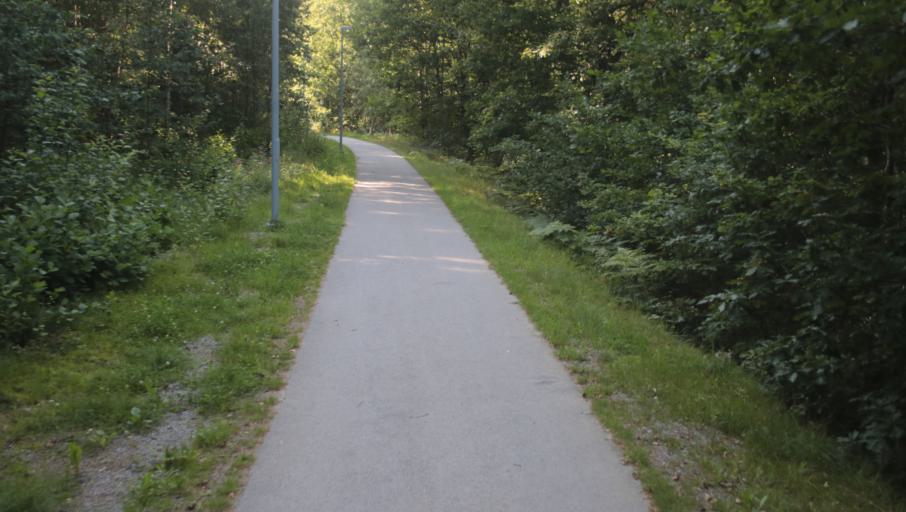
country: SE
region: Blekinge
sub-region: Karlshamns Kommun
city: Svangsta
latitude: 56.2543
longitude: 14.7871
